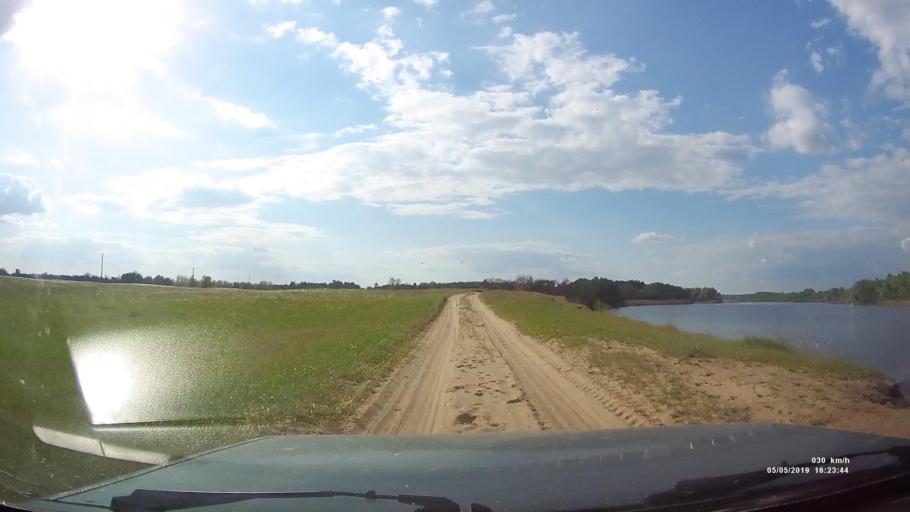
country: RU
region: Rostov
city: Konstantinovsk
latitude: 47.7573
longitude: 41.0293
